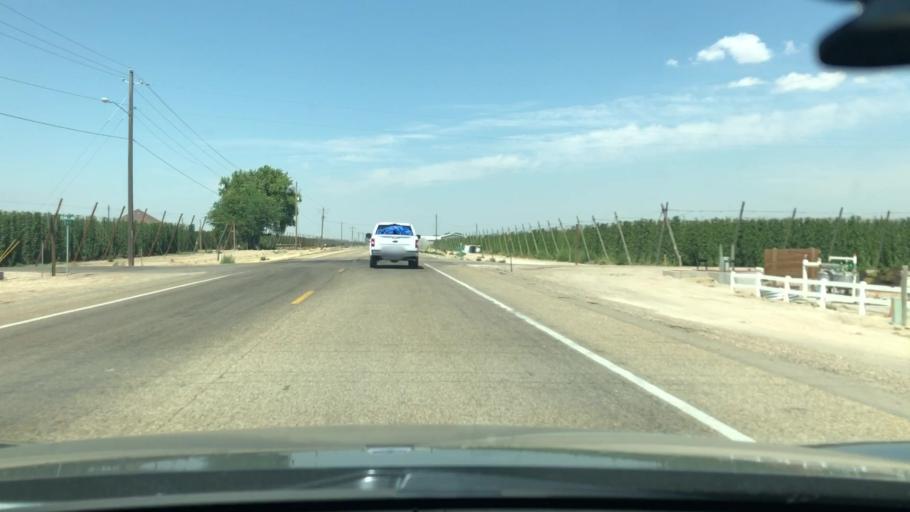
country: US
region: Idaho
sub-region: Canyon County
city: Wilder
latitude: 43.6976
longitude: -116.9119
